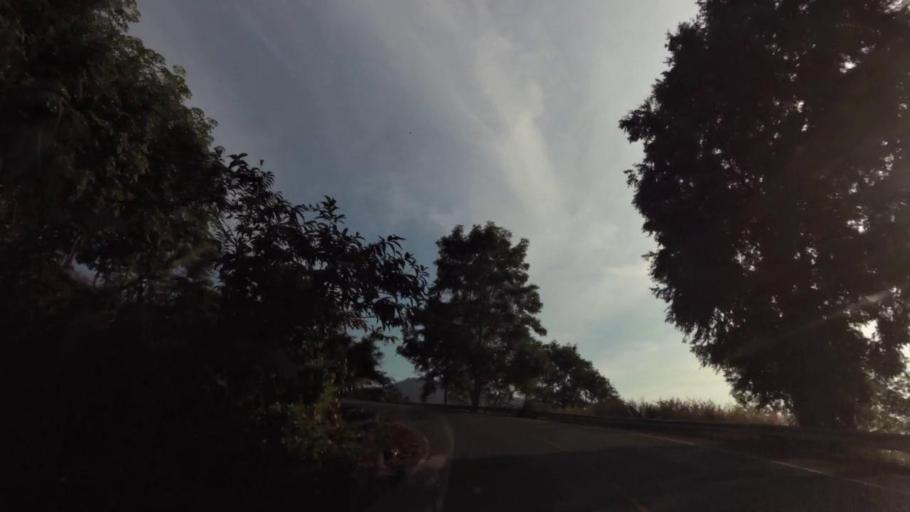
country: TH
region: Chiang Rai
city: Khun Tan
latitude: 19.8638
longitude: 100.4180
